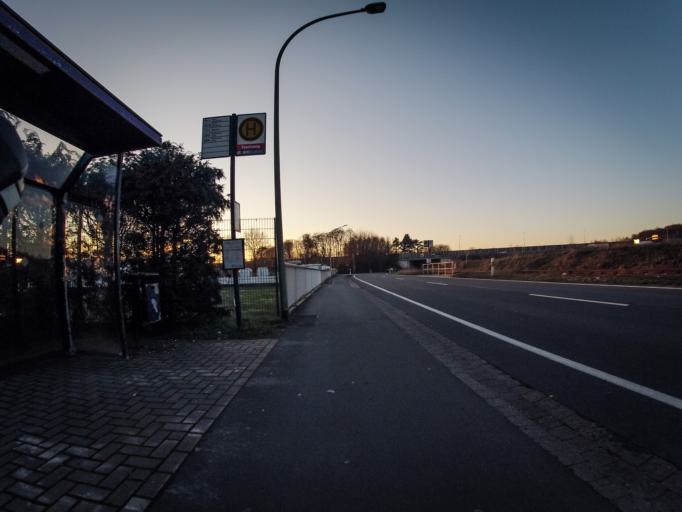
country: DE
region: North Rhine-Westphalia
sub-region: Regierungsbezirk Munster
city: Lotte
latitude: 52.3099
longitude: 7.9517
